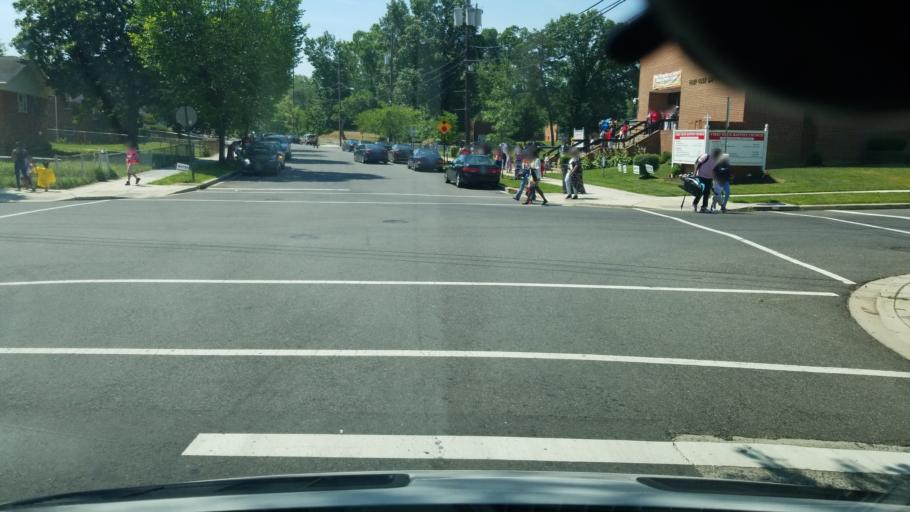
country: US
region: Maryland
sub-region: Prince George's County
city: Coral Hills
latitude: 38.8803
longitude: -76.9393
